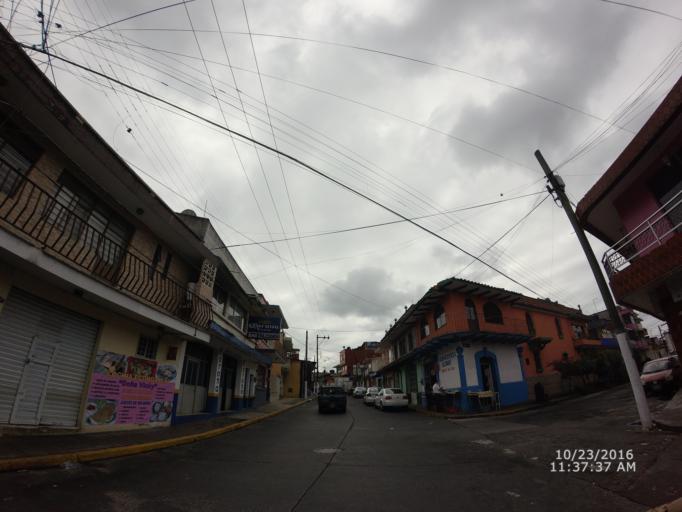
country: MX
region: Veracruz
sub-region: Xalapa
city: Xalapa de Enriquez
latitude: 19.5345
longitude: -96.9282
